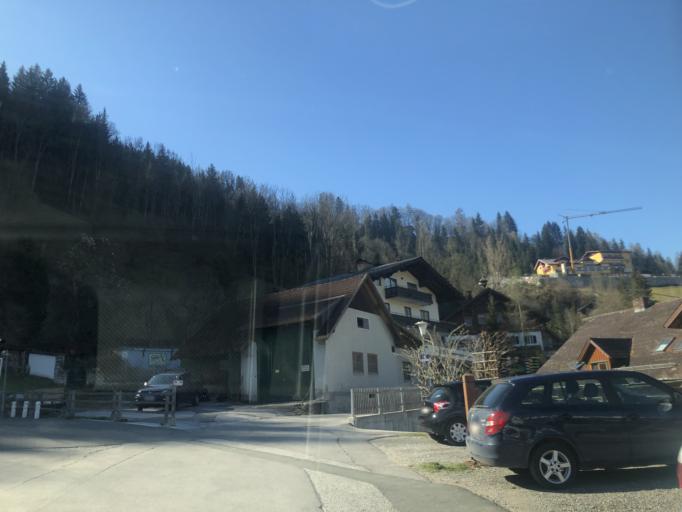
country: AT
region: Styria
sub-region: Politischer Bezirk Liezen
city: Schladming
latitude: 47.3896
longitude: 13.6889
